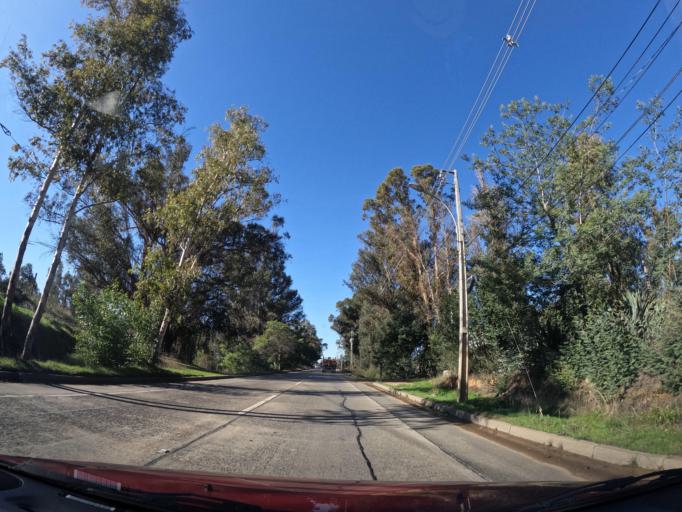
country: CL
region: Maule
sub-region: Provincia de Cauquenes
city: Cauquenes
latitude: -35.9576
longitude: -72.2814
